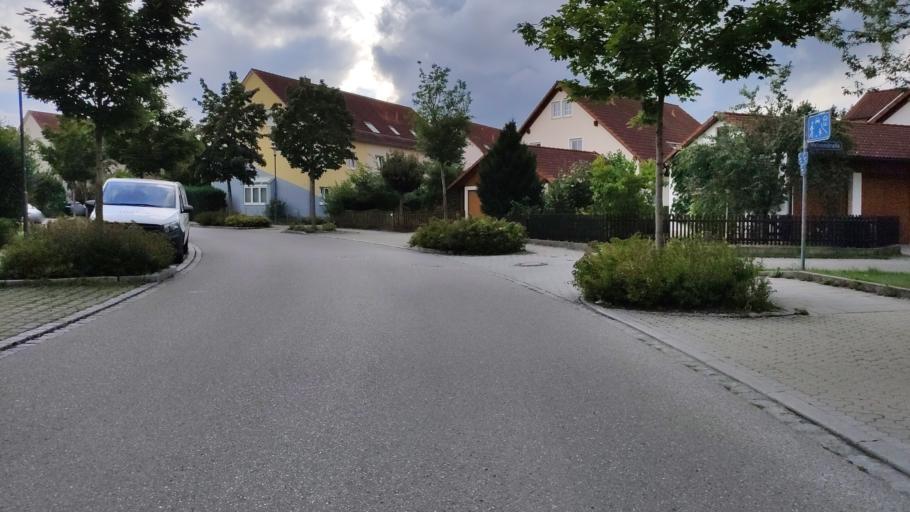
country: DE
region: Bavaria
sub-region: Swabia
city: Konigsbrunn
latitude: 48.2567
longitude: 10.8864
